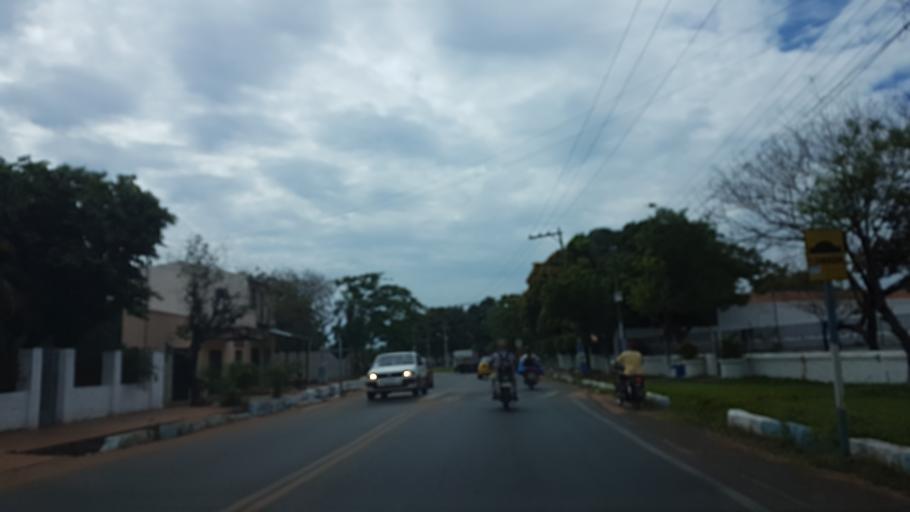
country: PY
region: Central
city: San Lorenzo
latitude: -25.2984
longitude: -57.4715
